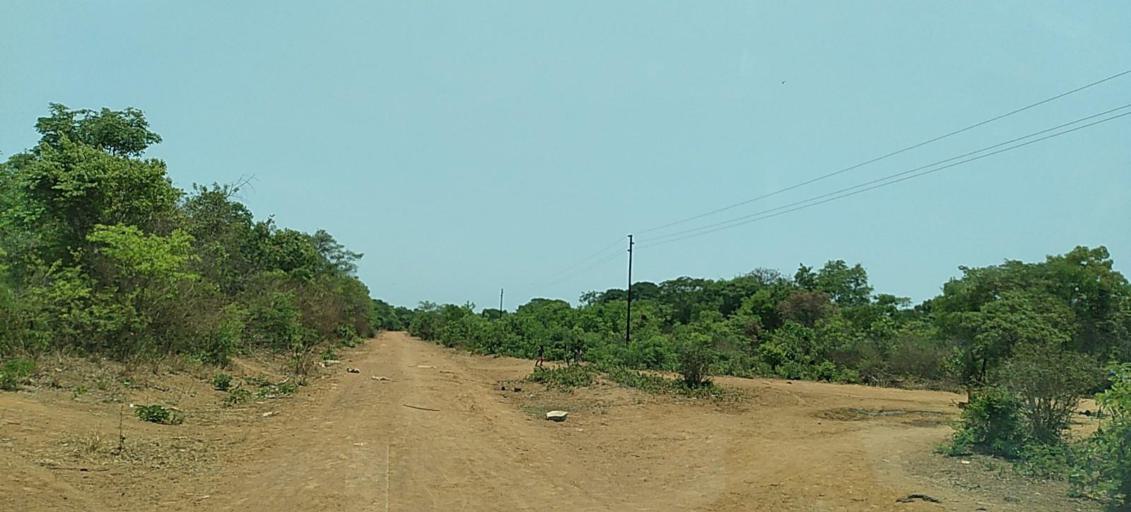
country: ZM
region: Copperbelt
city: Mpongwe
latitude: -13.8253
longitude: 27.8397
